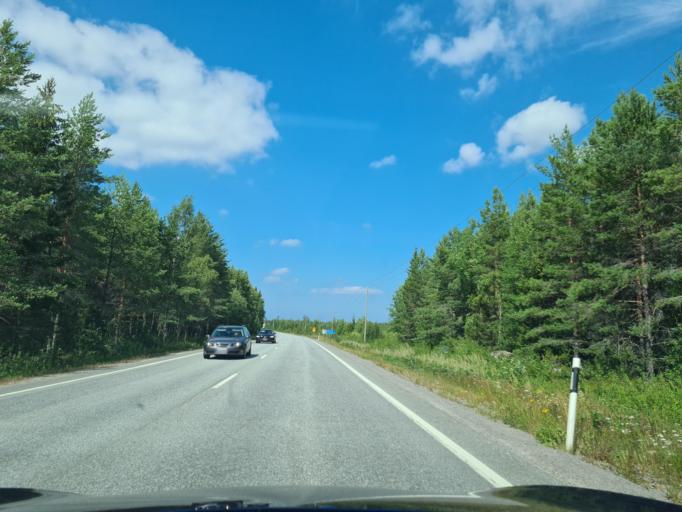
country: FI
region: Ostrobothnia
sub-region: Vaasa
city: Vaasa
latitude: 63.1624
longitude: 21.5912
